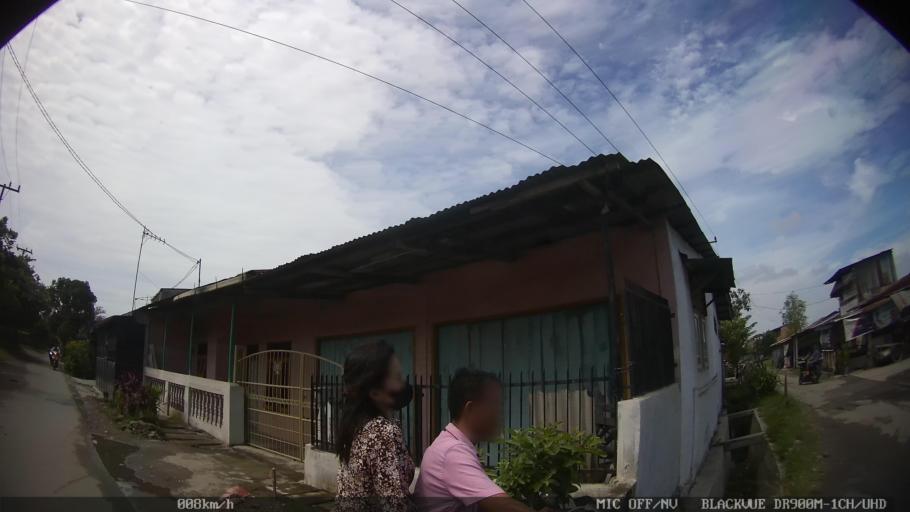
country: ID
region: North Sumatra
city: Medan
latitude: 3.5921
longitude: 98.7409
